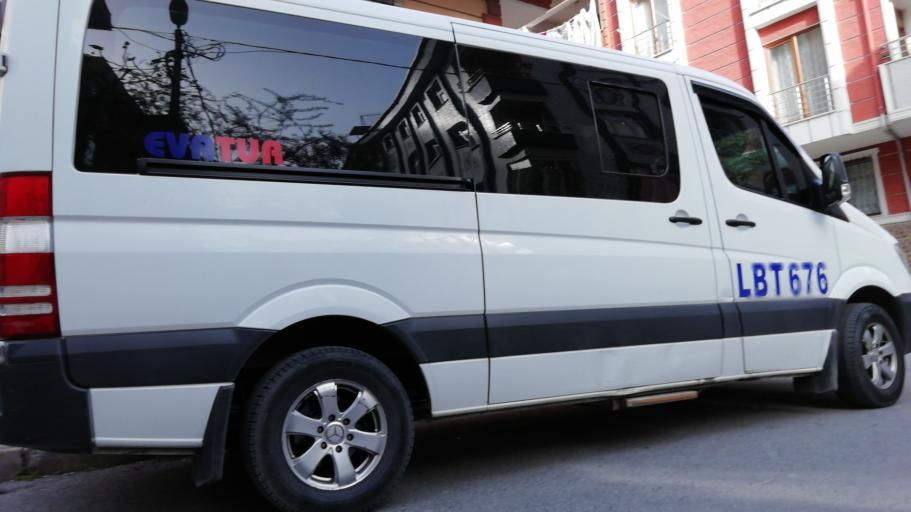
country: TR
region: Istanbul
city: Bagcilar
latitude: 41.0274
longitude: 28.8423
